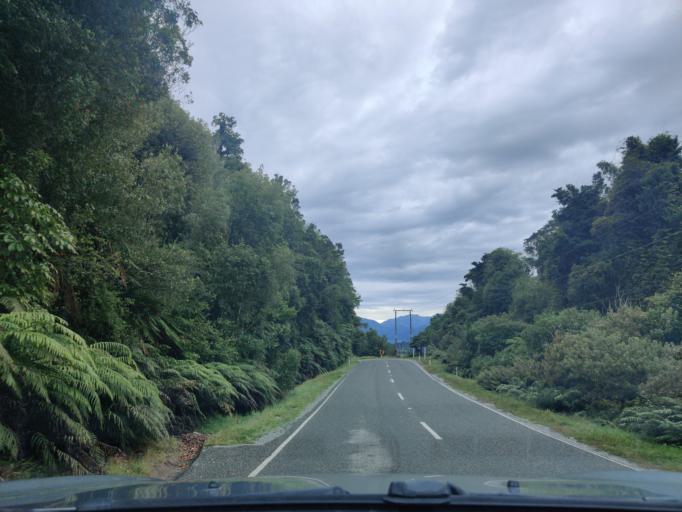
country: NZ
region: West Coast
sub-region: Westland District
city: Hokitika
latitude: -43.1616
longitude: 170.4739
